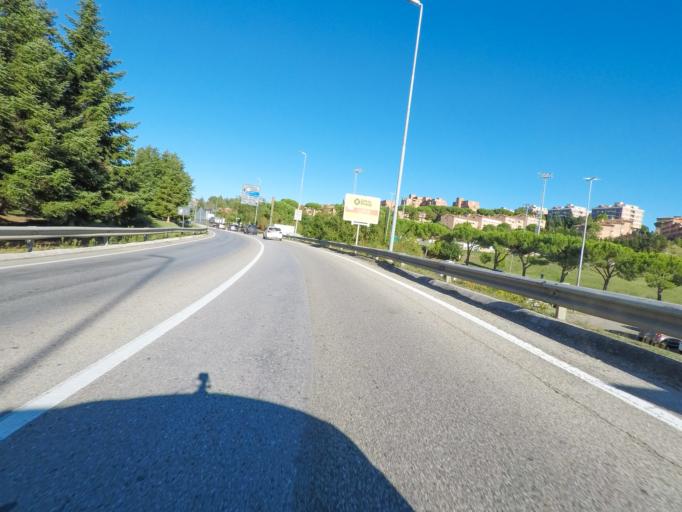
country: IT
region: Tuscany
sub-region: Provincia di Siena
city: Belverde
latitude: 43.3362
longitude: 11.2959
